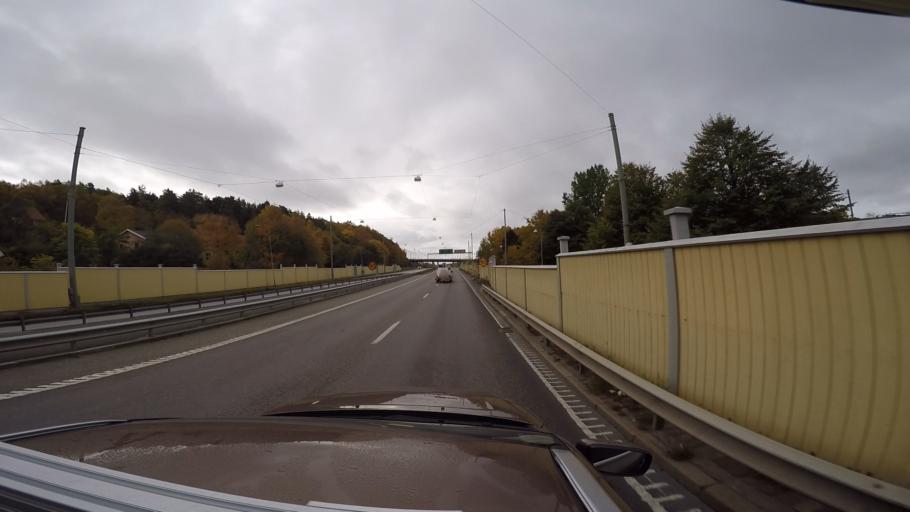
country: SE
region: Vaestra Goetaland
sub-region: Goteborg
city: Majorna
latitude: 57.6748
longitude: 11.9396
